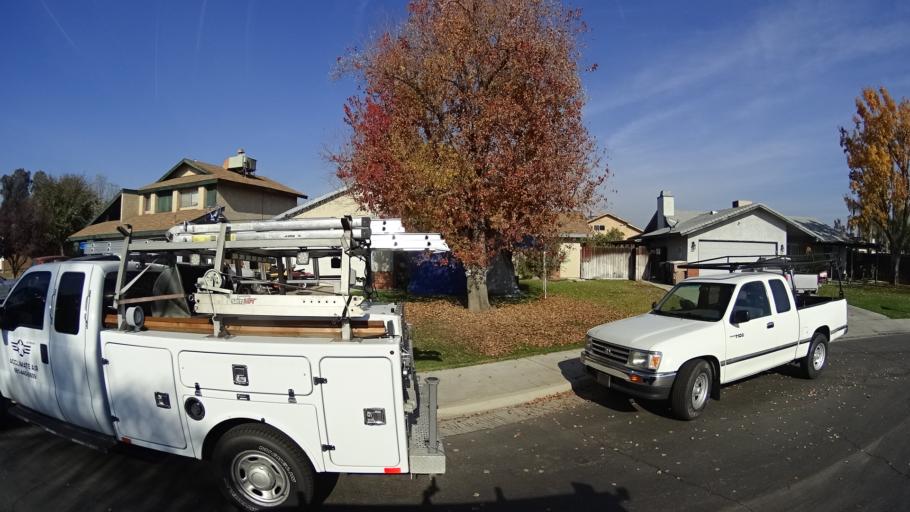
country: US
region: California
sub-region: Kern County
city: Greenfield
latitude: 35.3023
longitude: -119.0305
